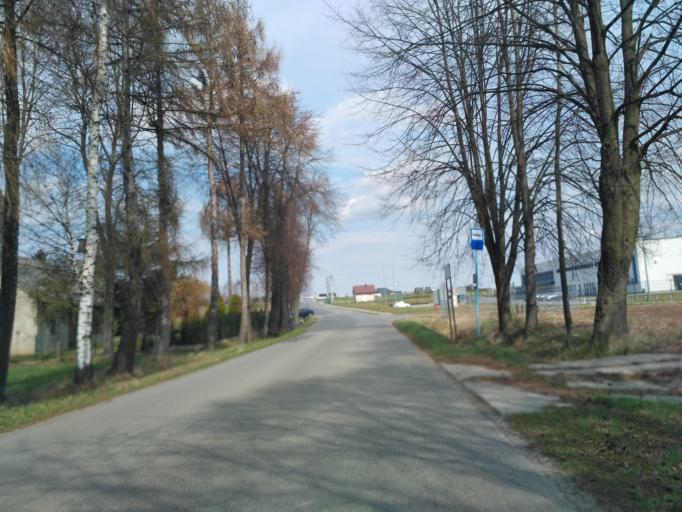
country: PL
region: Subcarpathian Voivodeship
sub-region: Powiat ropczycko-sedziszowski
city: Sedziszow Malopolski
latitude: 50.0597
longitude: 21.7146
